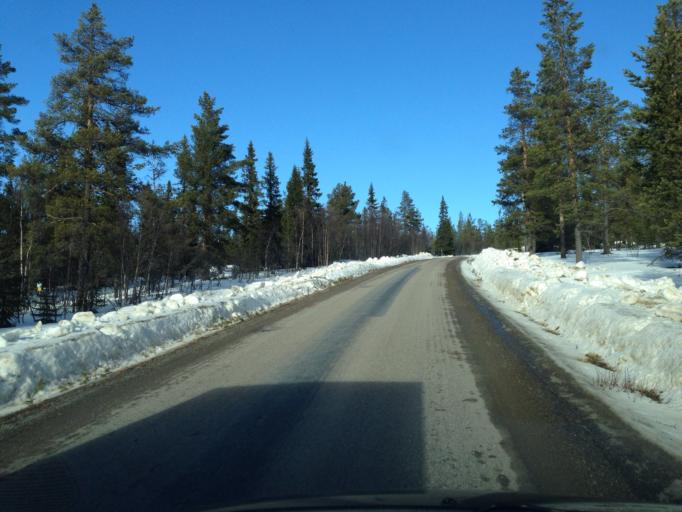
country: SE
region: Jaemtland
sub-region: Harjedalens Kommun
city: Sveg
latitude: 62.1303
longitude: 13.2632
